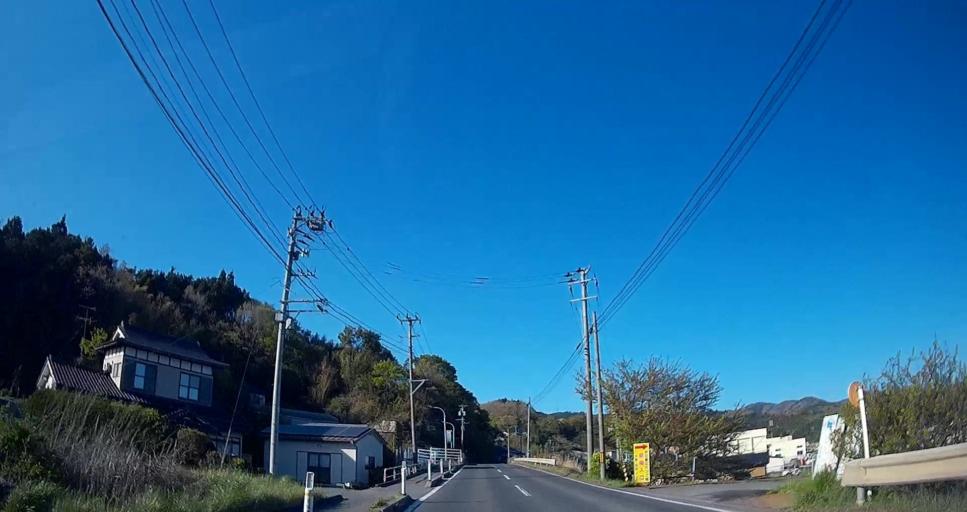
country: JP
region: Miyagi
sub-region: Oshika Gun
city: Onagawa Cho
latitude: 38.4310
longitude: 141.3809
